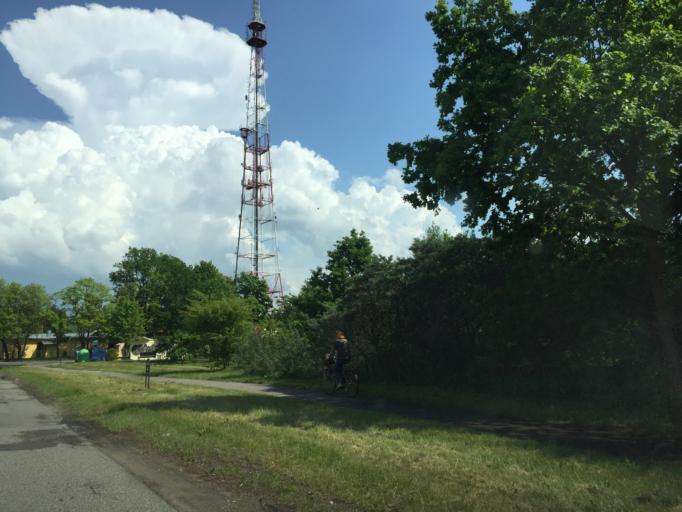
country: LT
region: Klaipedos apskritis
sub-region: Klaipeda
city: Klaipeda
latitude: 55.7694
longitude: 21.0932
